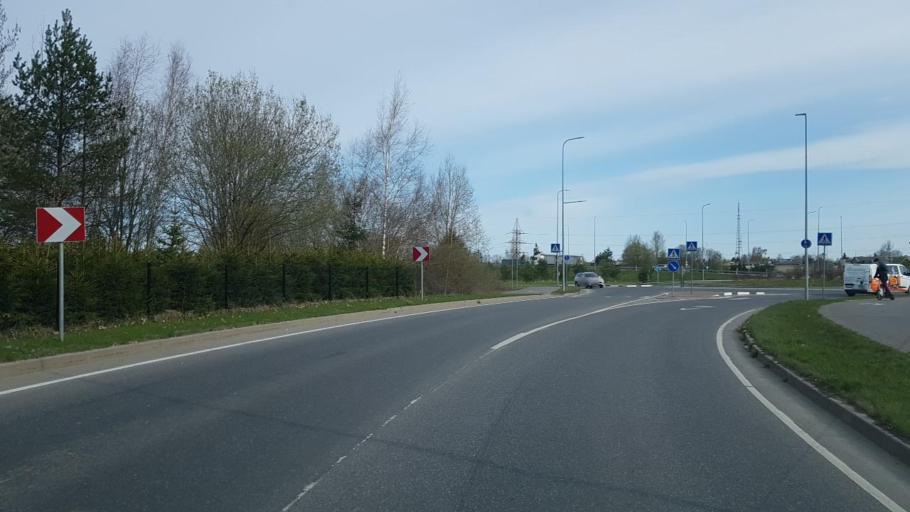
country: EE
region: Tartu
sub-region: UElenurme vald
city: Ulenurme
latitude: 58.3439
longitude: 26.6993
